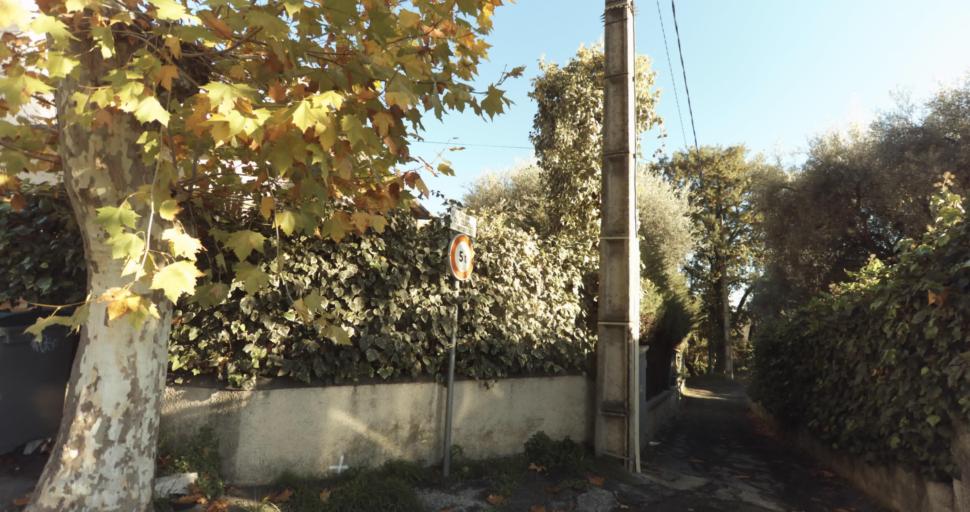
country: FR
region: Provence-Alpes-Cote d'Azur
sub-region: Departement des Alpes-Maritimes
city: Vence
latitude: 43.7267
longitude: 7.1110
